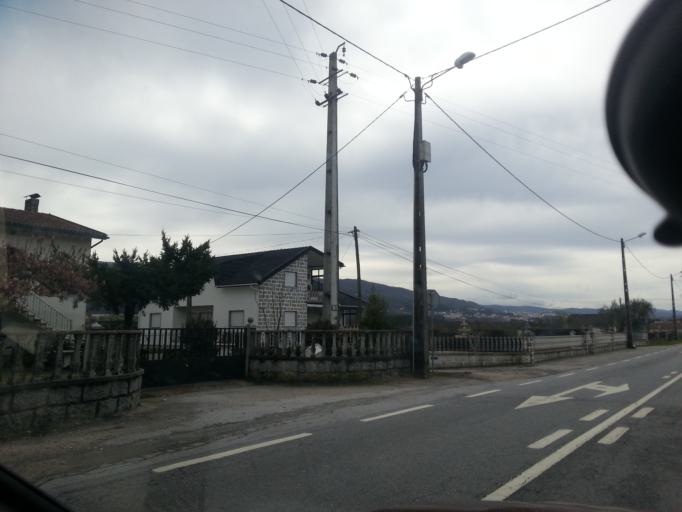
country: PT
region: Guarda
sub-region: Seia
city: Seia
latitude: 40.4634
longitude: -7.6878
